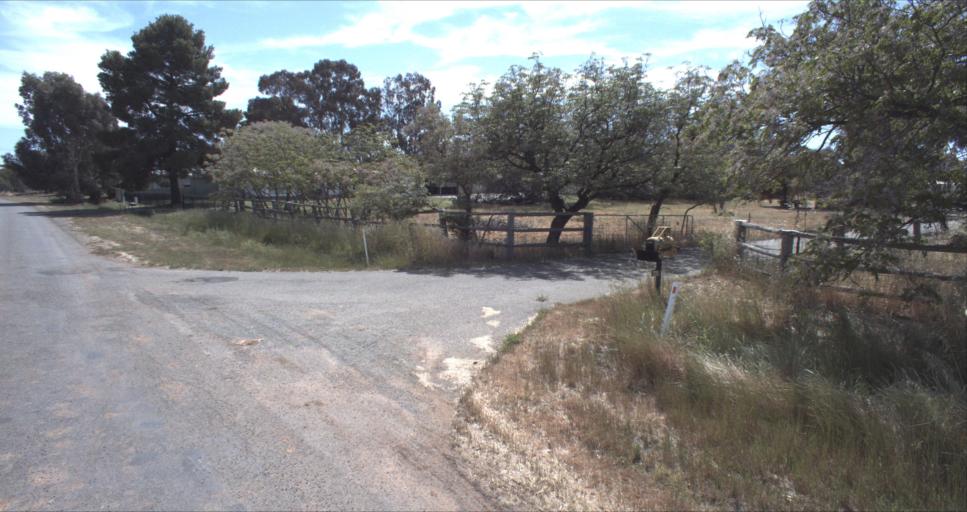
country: AU
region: New South Wales
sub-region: Leeton
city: Leeton
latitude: -34.5704
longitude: 146.4560
